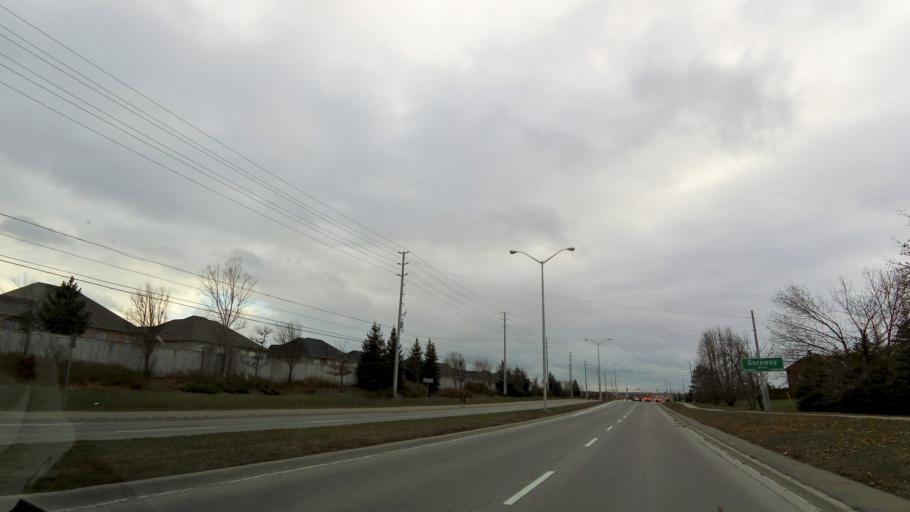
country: CA
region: Ontario
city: Brampton
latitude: 43.7750
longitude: -79.7091
